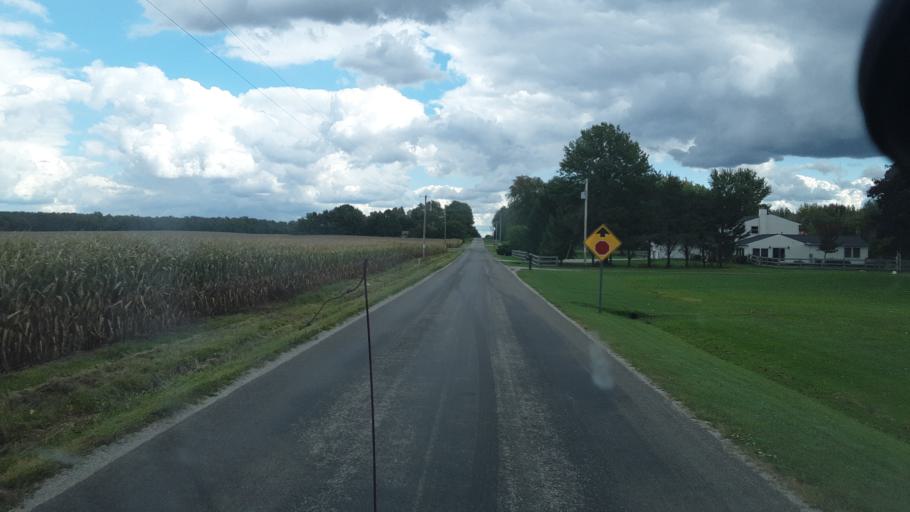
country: US
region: Ohio
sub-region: Knox County
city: Centerburg
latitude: 40.2331
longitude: -82.7565
